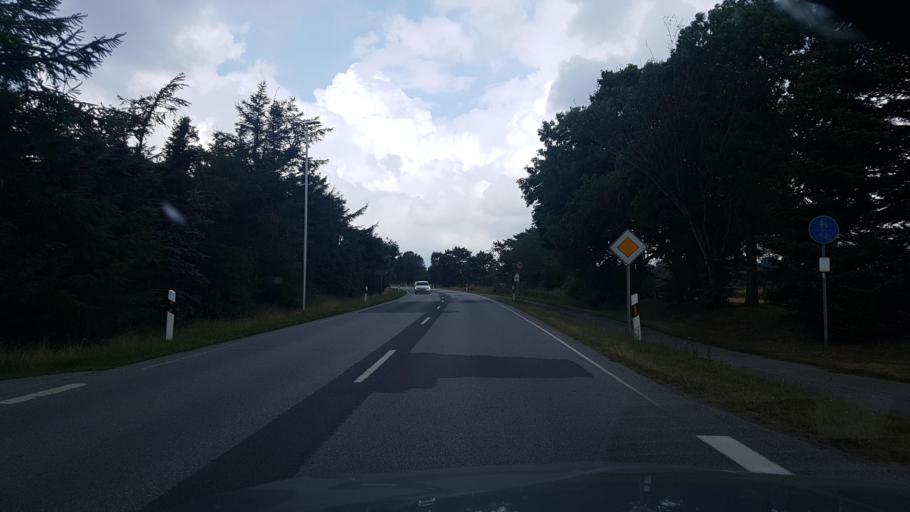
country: DE
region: Schleswig-Holstein
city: Schobull
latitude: 54.4967
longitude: 9.0264
